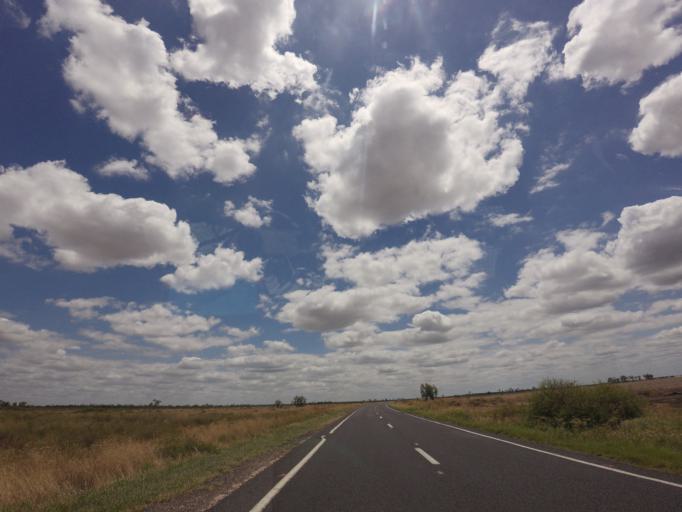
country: AU
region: New South Wales
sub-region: Moree Plains
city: Boggabilla
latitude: -28.7051
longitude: 150.2804
